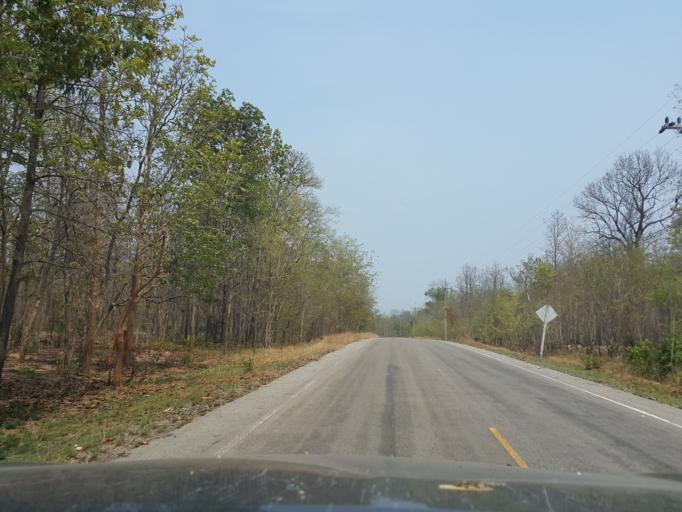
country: TH
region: Lampang
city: Mae Phrik
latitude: 17.5579
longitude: 99.1017
